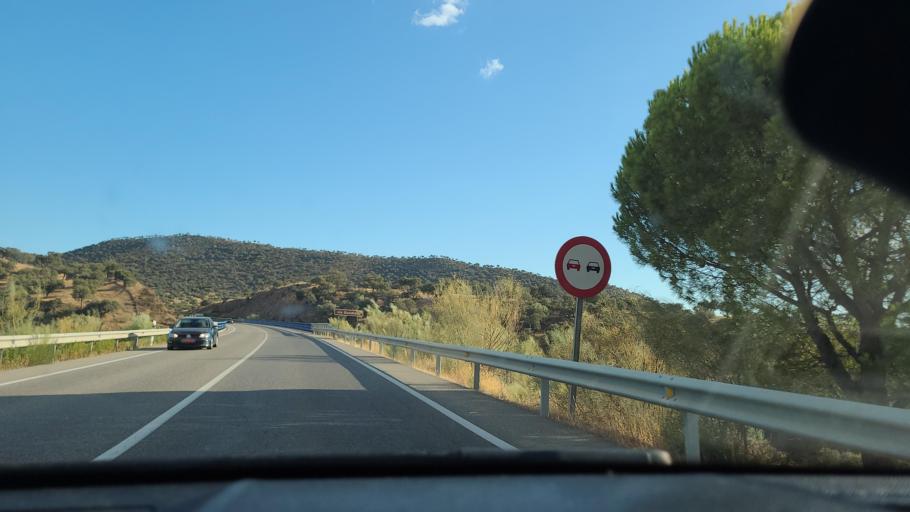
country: ES
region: Andalusia
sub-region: Province of Cordoba
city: Belmez
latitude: 38.2349
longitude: -5.1679
